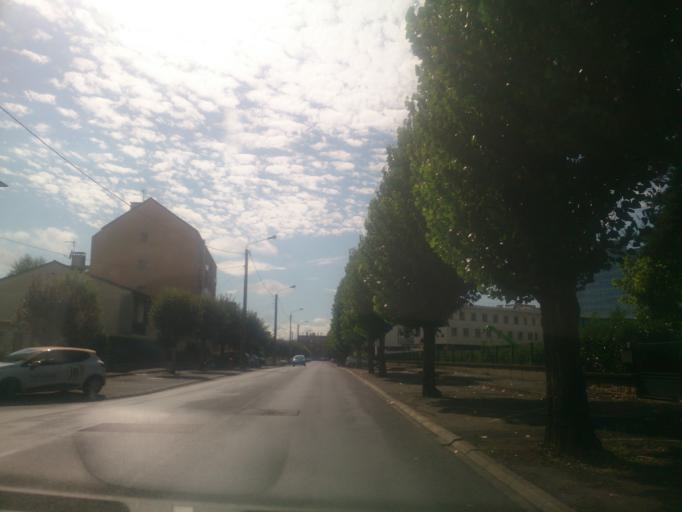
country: FR
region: Limousin
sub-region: Departement de la Correze
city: Brive-la-Gaillarde
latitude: 45.1682
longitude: 1.5369
